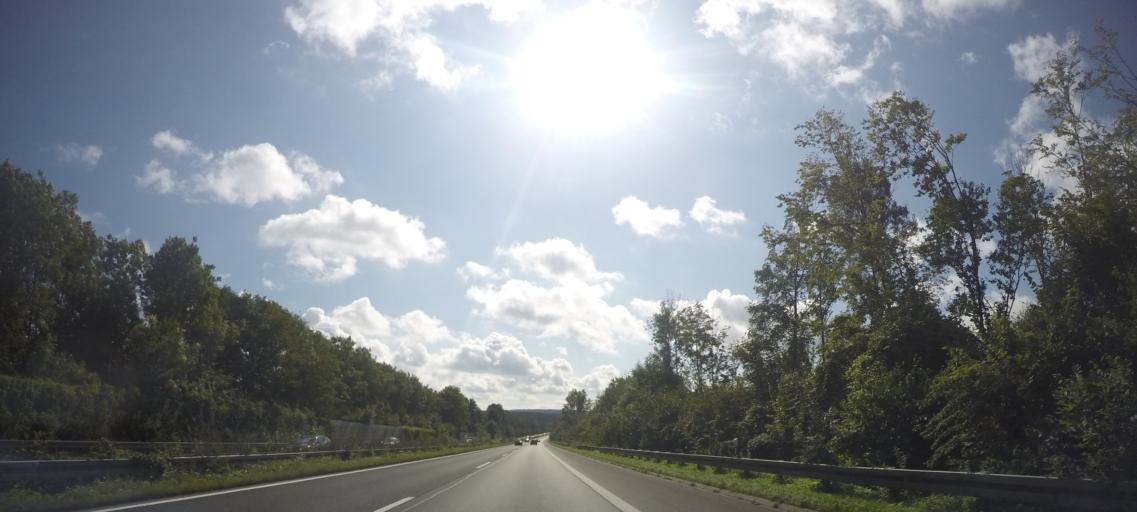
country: DE
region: North Rhine-Westphalia
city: Wickede
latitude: 51.5044
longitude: 7.9150
